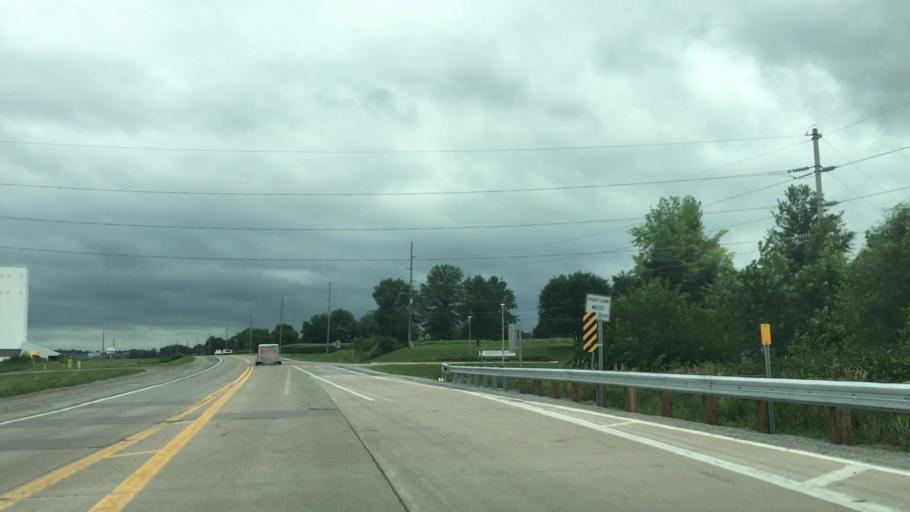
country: US
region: Iowa
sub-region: Johnson County
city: Tiffin
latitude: 41.7017
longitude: -91.6309
